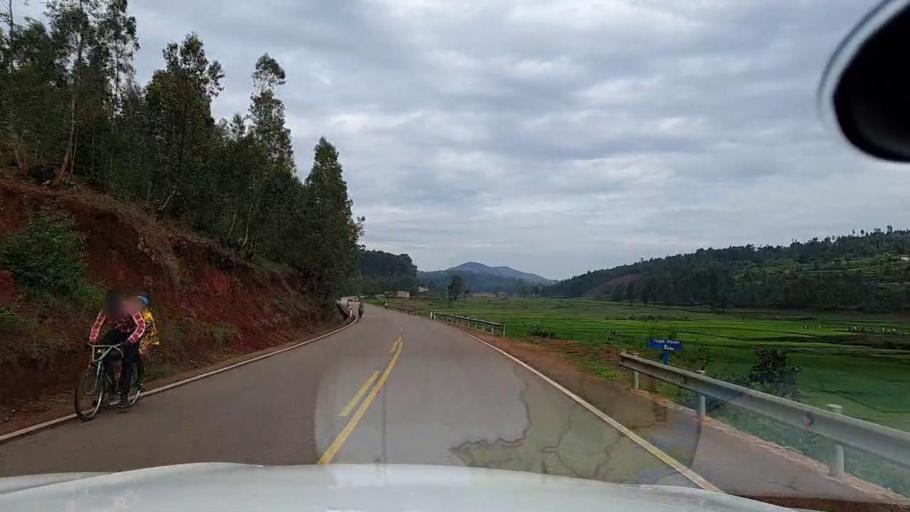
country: RW
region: Southern Province
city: Butare
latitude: -2.5674
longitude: 29.7278
